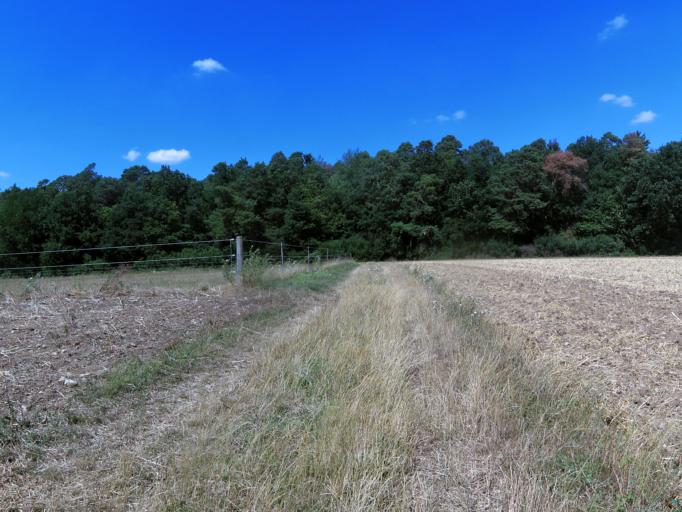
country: DE
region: Bavaria
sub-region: Regierungsbezirk Unterfranken
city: Gadheim
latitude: 49.8320
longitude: 9.9120
